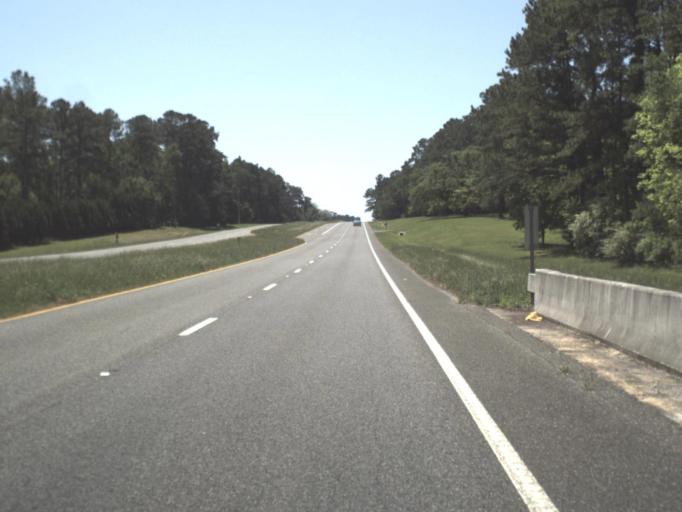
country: US
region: Florida
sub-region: Jefferson County
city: Monticello
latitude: 30.6007
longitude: -83.8716
